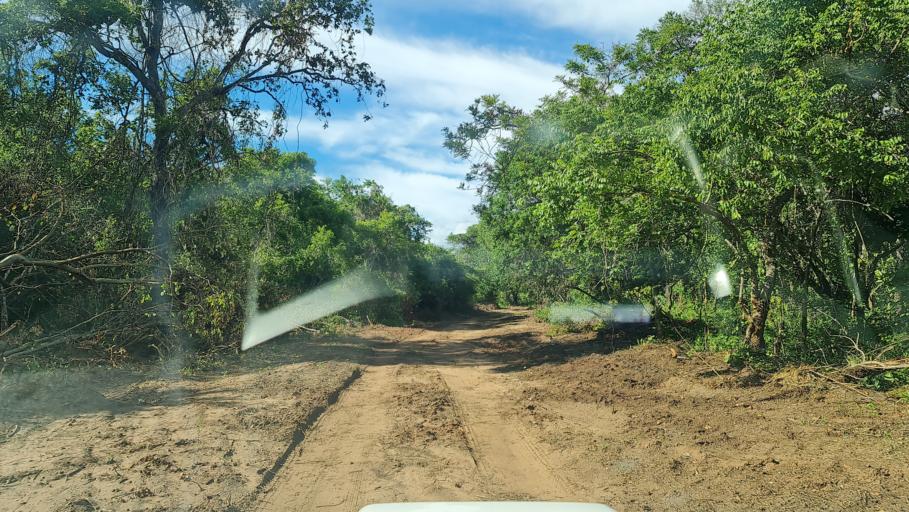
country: MZ
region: Nampula
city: Antonio Enes
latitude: -15.5283
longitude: 40.1267
